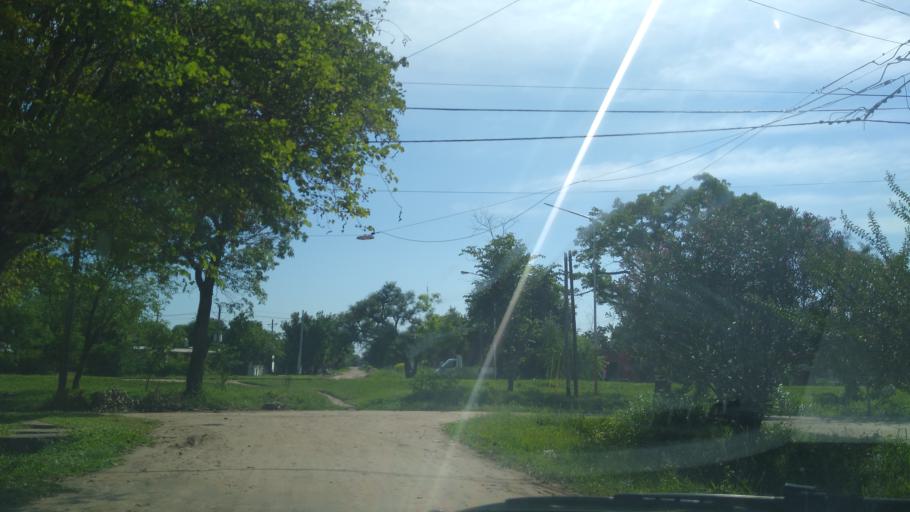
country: AR
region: Chaco
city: Barranqueras
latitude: -27.4876
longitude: -58.9535
